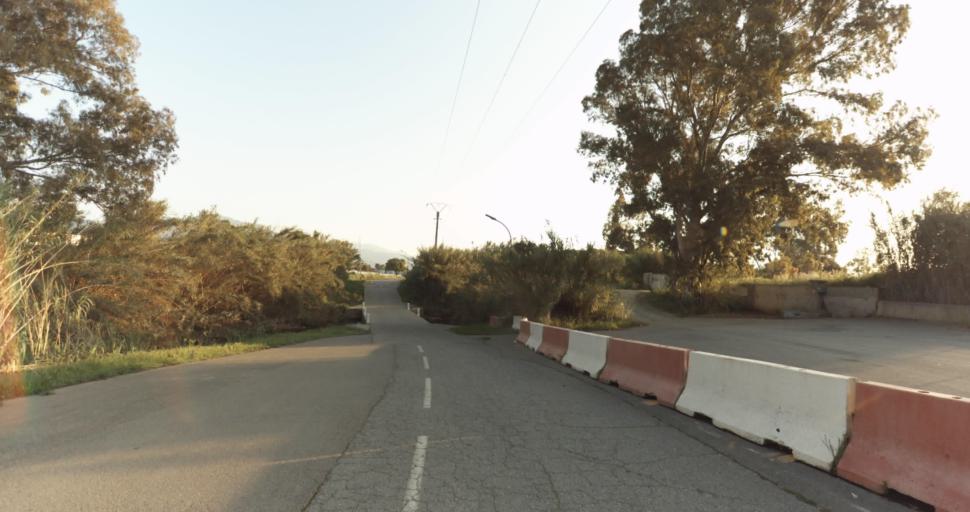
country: FR
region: Corsica
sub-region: Departement de la Haute-Corse
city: Biguglia
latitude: 42.6158
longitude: 9.4434
